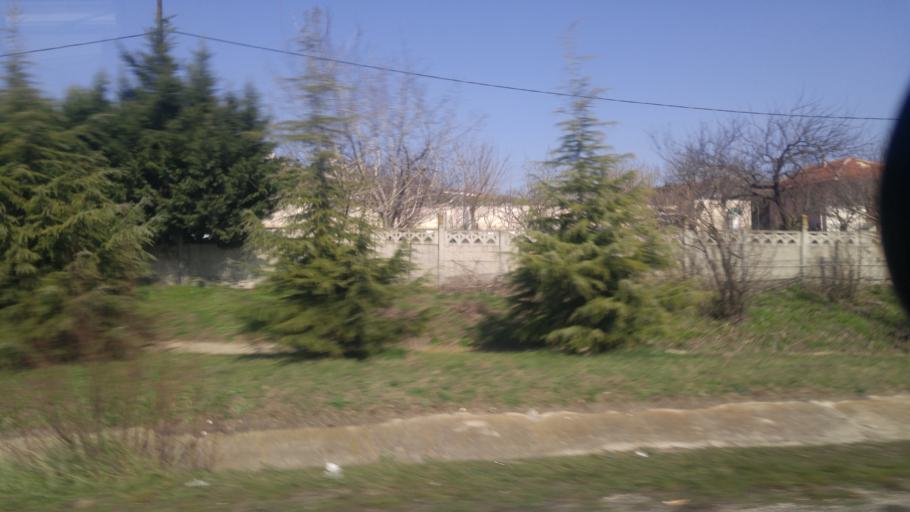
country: TR
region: Istanbul
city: Celaliye
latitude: 41.0591
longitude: 28.4131
